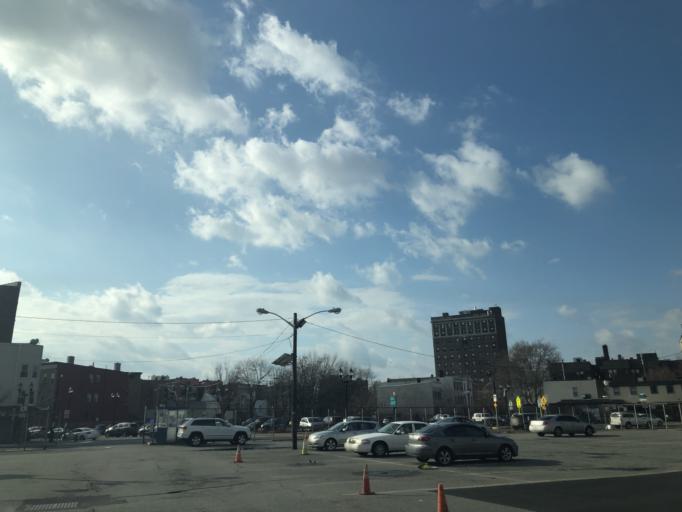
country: US
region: New Jersey
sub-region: Hudson County
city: Jersey City
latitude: 40.7252
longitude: -74.0663
